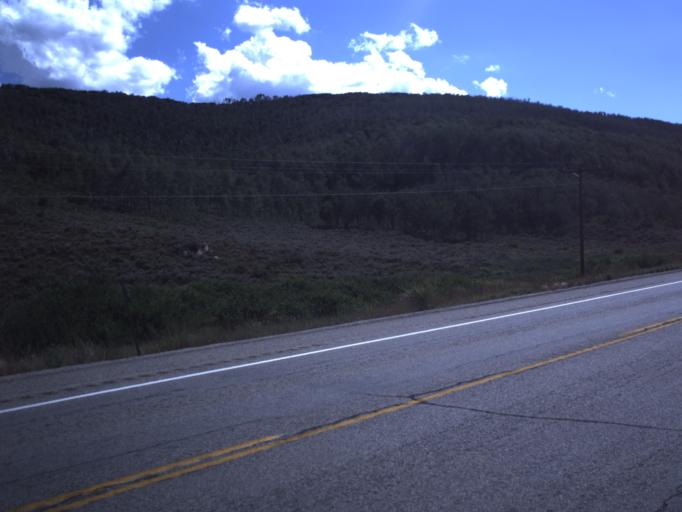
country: US
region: Utah
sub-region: Summit County
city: Francis
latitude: 40.2014
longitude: -110.9875
